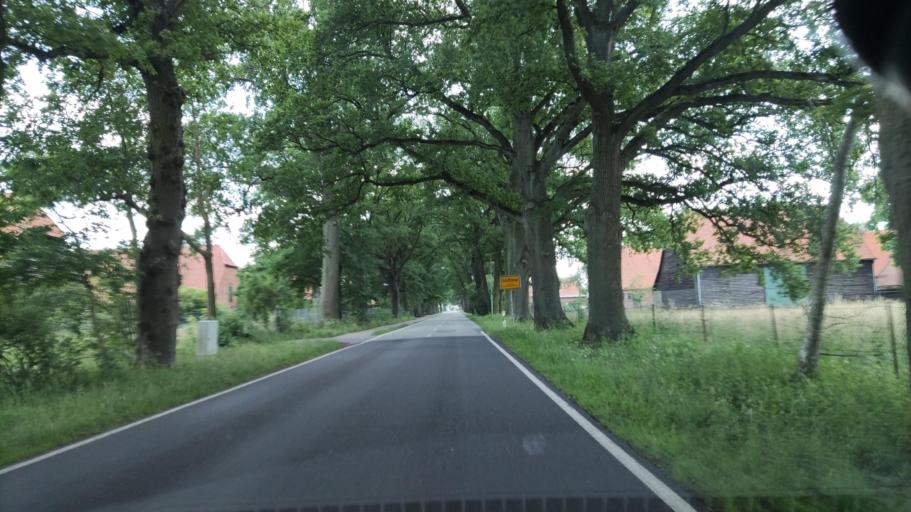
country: DE
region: Mecklenburg-Vorpommern
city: Lubtheen
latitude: 53.3425
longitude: 11.1428
